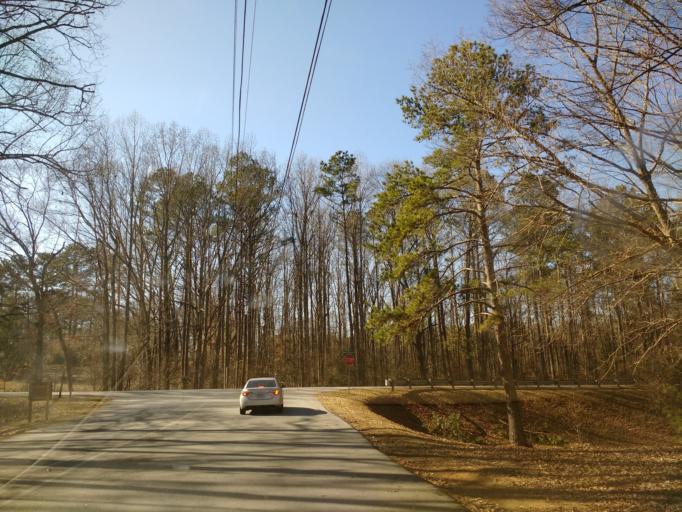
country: US
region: Georgia
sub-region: Douglas County
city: Lithia Springs
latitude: 33.7542
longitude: -84.6392
